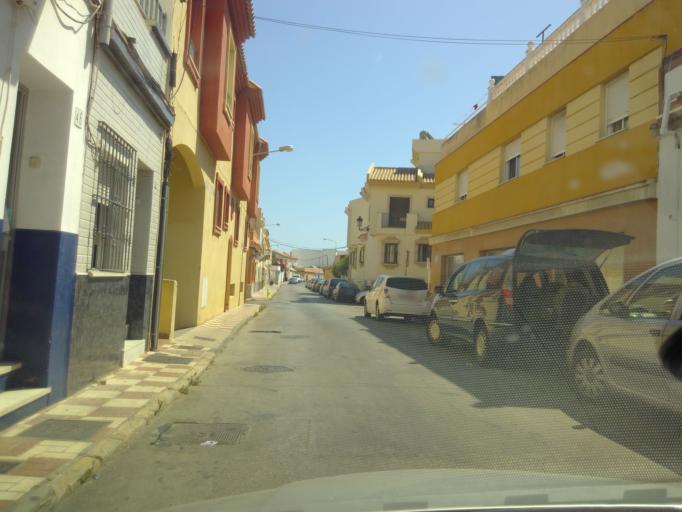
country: ES
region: Andalusia
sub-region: Provincia de Cadiz
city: La Linea de la Concepcion
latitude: 36.1678
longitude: -5.3490
